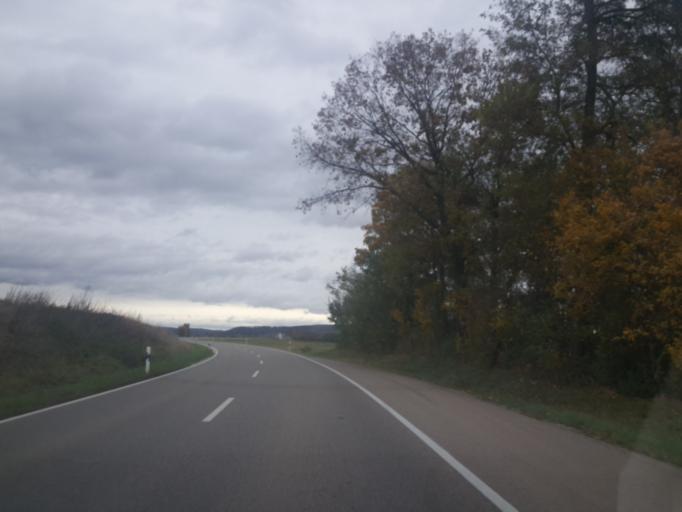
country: DE
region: Bavaria
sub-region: Upper Bavaria
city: Rennertshofen
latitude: 48.7462
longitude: 11.0304
